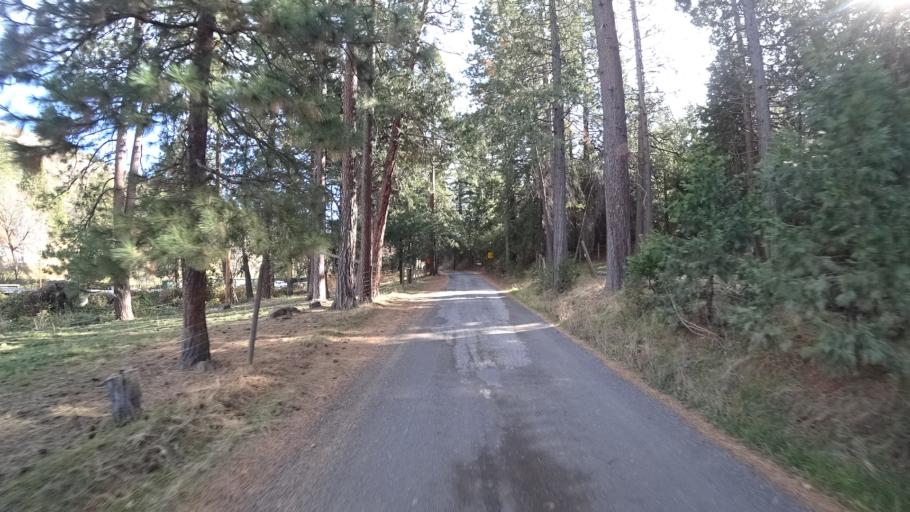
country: US
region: California
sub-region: Siskiyou County
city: Weed
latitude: 41.4313
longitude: -122.4012
